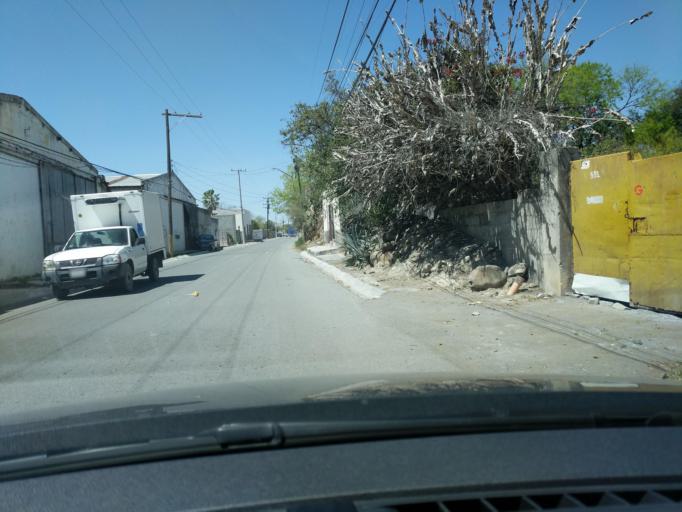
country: MX
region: Nuevo Leon
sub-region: Apodaca
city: Artemio Trevino
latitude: 25.8130
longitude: -100.1362
